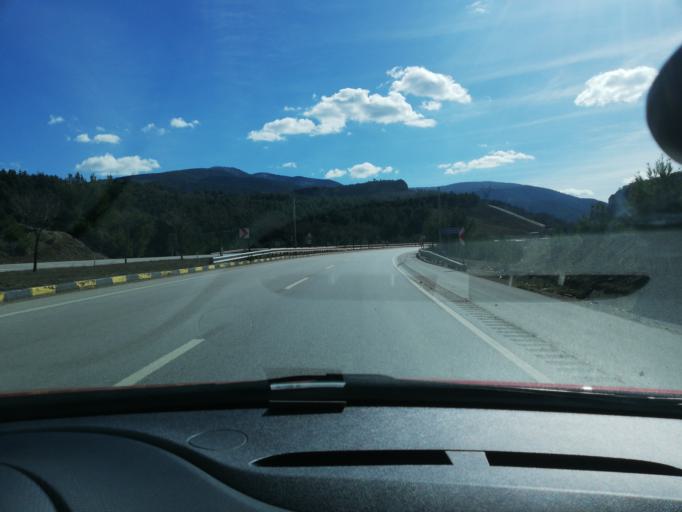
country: TR
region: Karabuk
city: Karabuk
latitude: 41.0923
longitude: 32.6786
